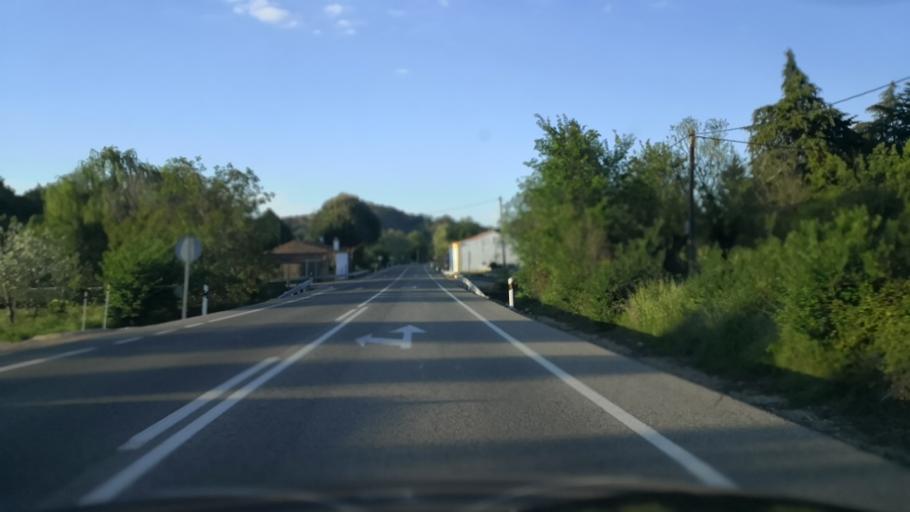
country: PT
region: Portalegre
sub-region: Portalegre
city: Sao Juliao
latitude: 39.3631
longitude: -7.2729
